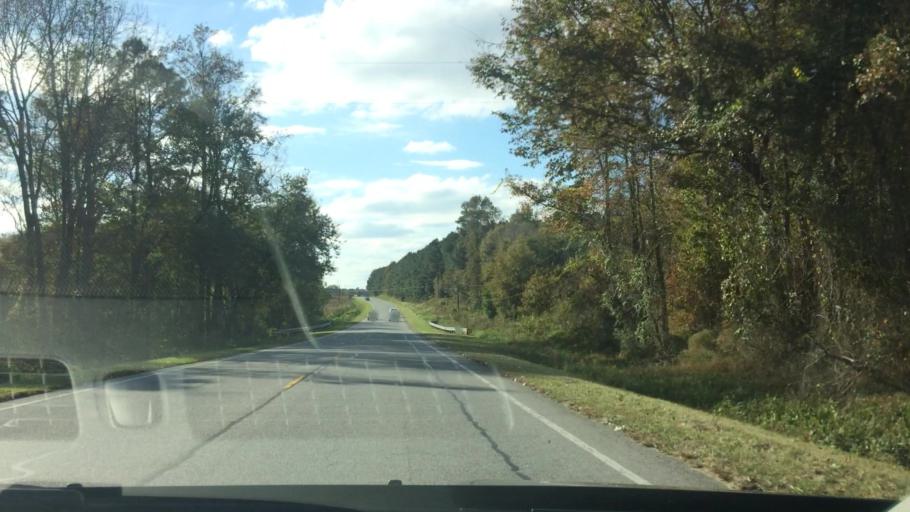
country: US
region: North Carolina
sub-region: Greene County
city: Snow Hill
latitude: 35.4418
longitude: -77.8157
